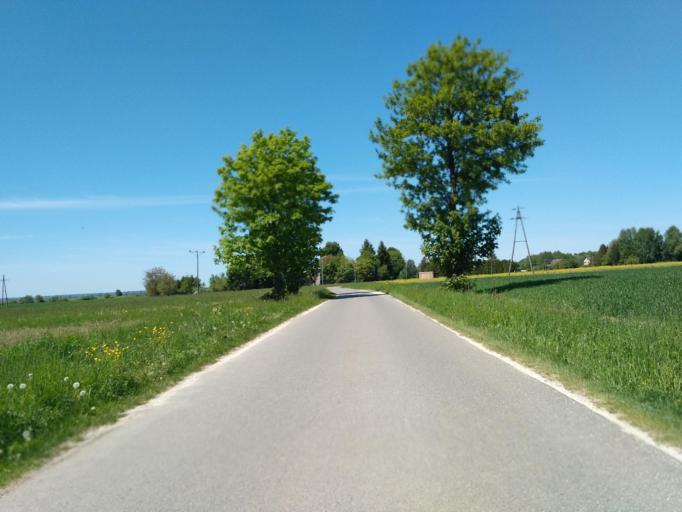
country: PL
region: Subcarpathian Voivodeship
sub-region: Powiat sanocki
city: Dlugie
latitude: 49.5958
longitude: 22.0457
